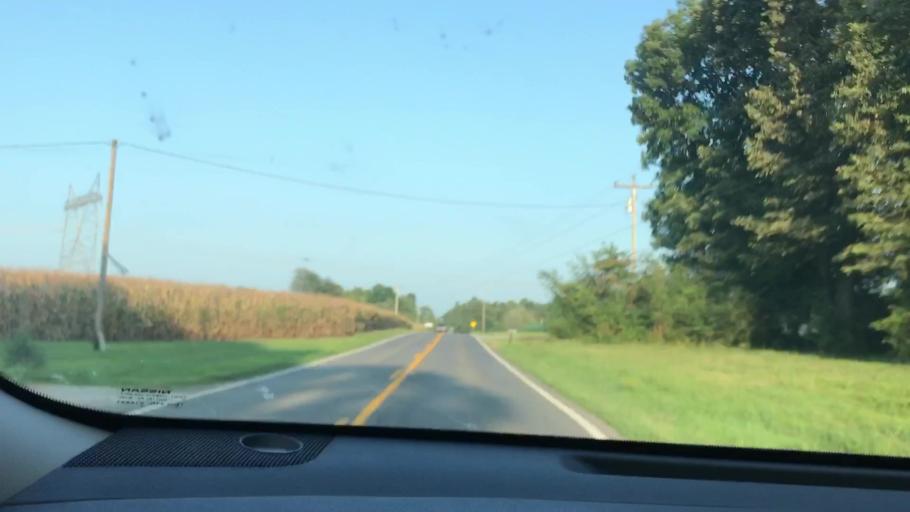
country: US
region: Kentucky
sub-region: Calloway County
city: Murray
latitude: 36.5805
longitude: -88.2442
